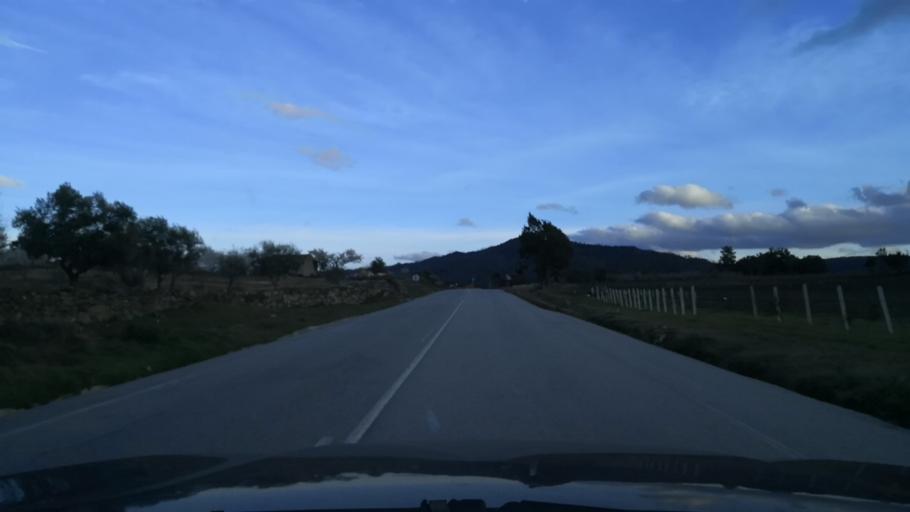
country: PT
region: Braganca
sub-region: Carrazeda de Ansiaes
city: Carrazeda de Anciaes
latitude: 41.2786
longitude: -7.3313
